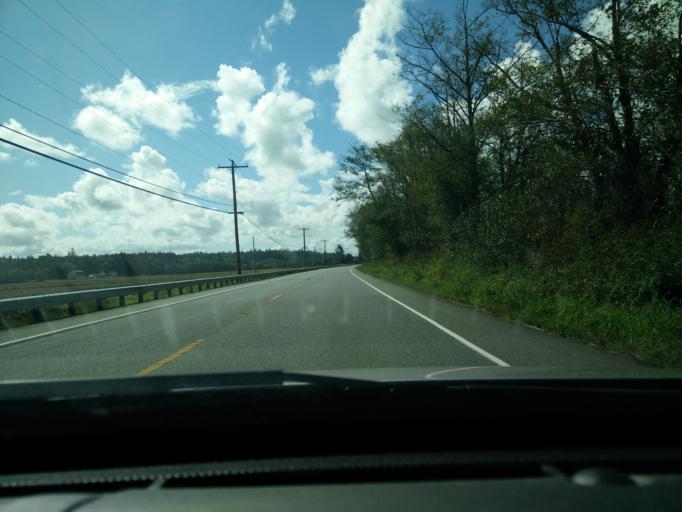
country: US
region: Washington
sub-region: Snohomish County
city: Stanwood
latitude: 48.3163
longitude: -122.3450
